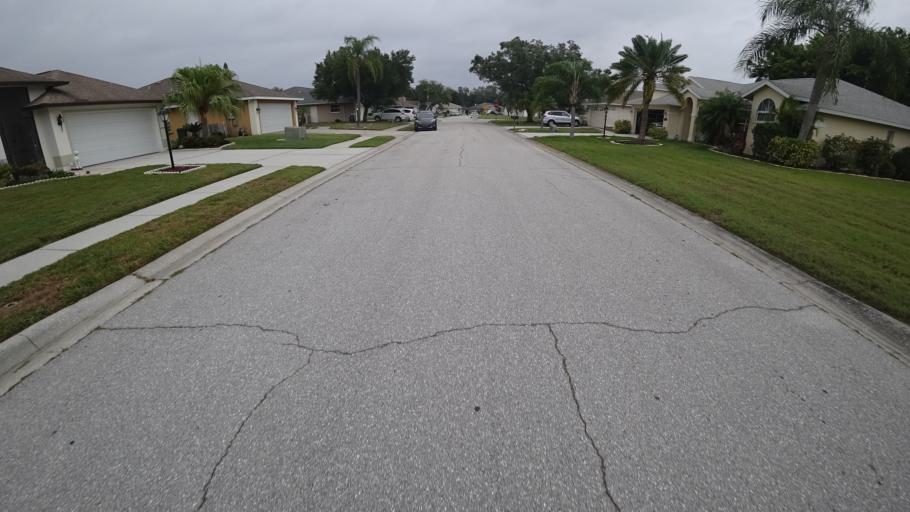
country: US
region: Florida
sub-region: Manatee County
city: Samoset
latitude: 27.4382
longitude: -82.5108
